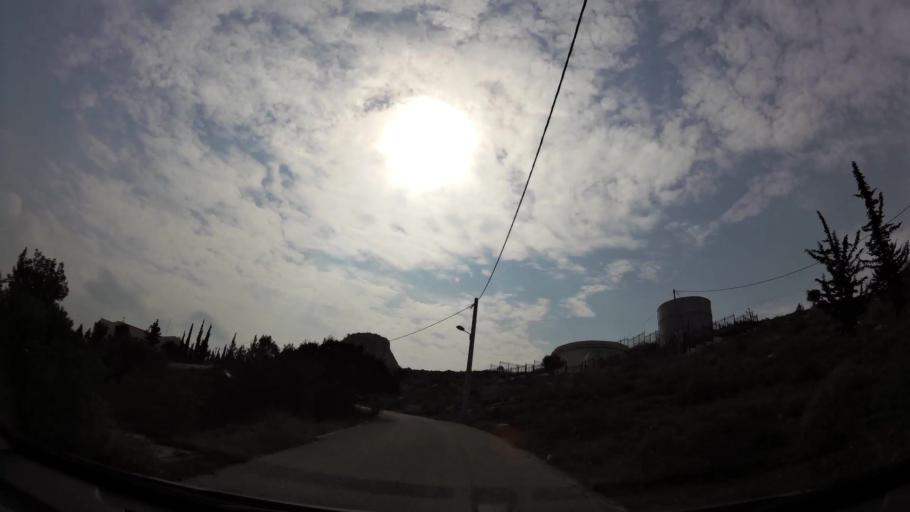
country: GR
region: Attica
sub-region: Nomarchia Athinas
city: Psychiko
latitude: 38.0151
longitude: 23.7634
